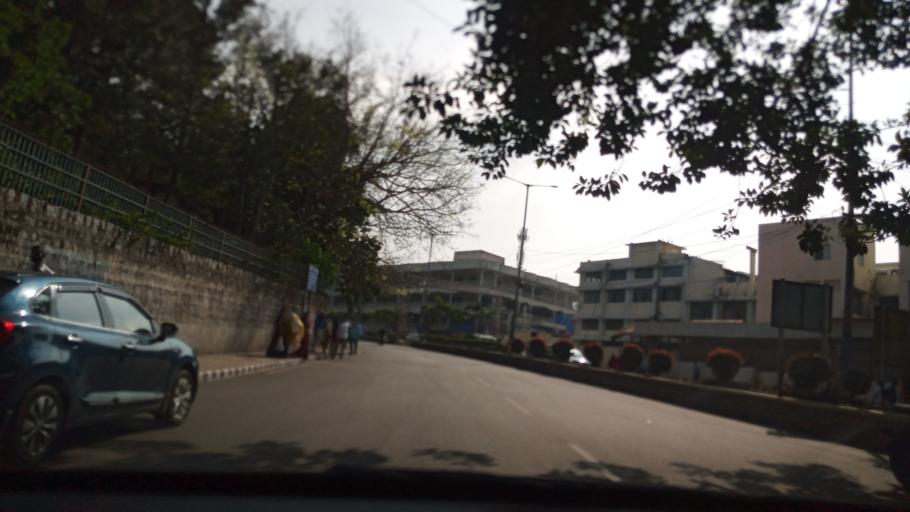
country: IN
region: Andhra Pradesh
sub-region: Chittoor
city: Tirumala
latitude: 13.6828
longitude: 79.3504
